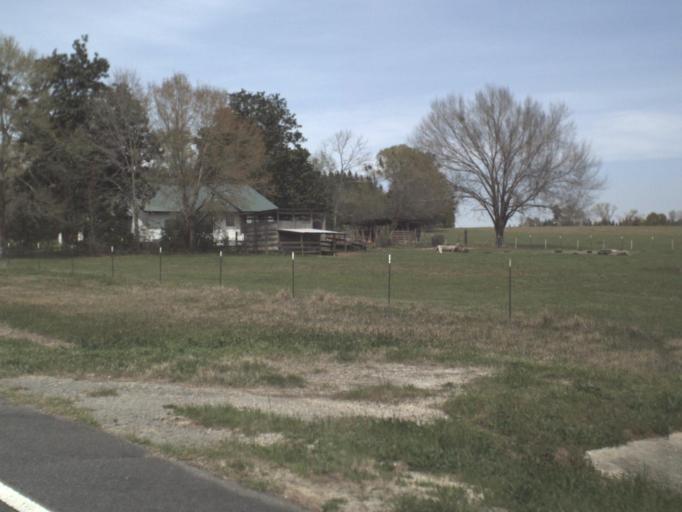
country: US
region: Alabama
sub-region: Geneva County
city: Geneva
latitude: 30.9520
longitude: -85.9844
